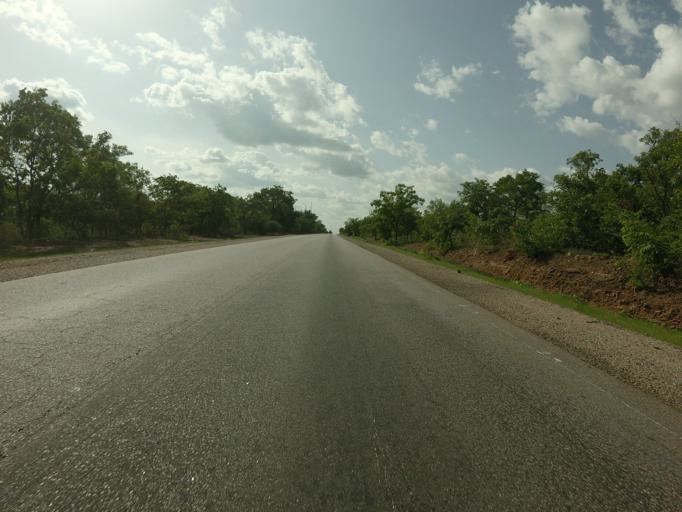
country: GH
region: Upper East
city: Bolgatanga
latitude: 10.5436
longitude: -0.8252
